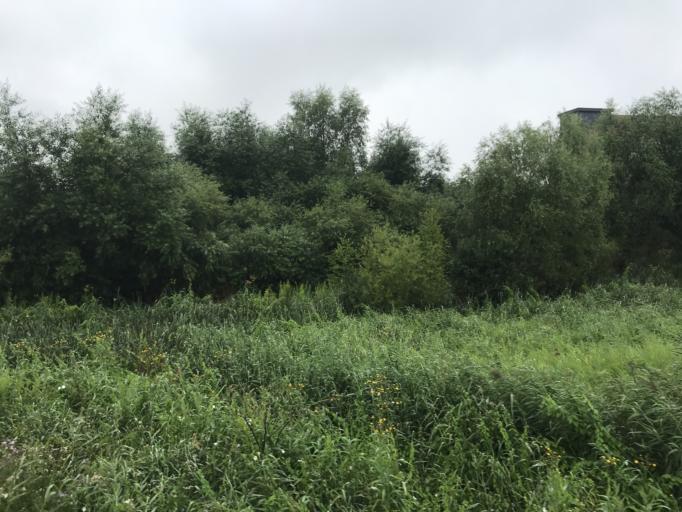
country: PL
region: Warmian-Masurian Voivodeship
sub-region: Powiat elblaski
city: Elblag
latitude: 54.1461
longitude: 19.3948
